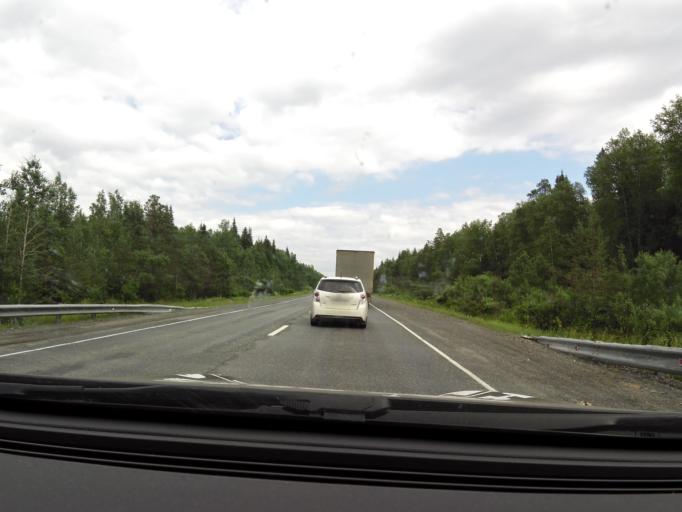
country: RU
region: Sverdlovsk
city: Nizhniye Sergi
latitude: 56.8237
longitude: 59.3015
